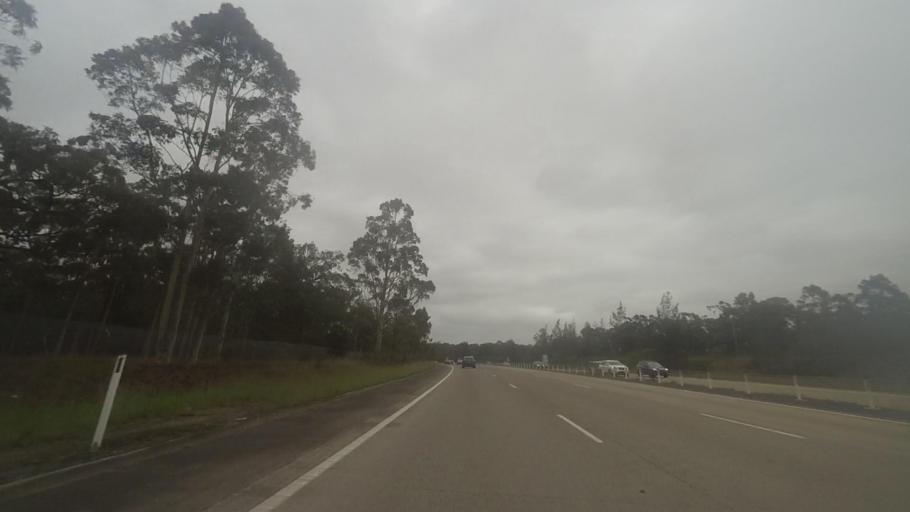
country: AU
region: New South Wales
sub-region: Port Stephens Shire
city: Medowie
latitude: -32.6843
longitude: 151.8120
